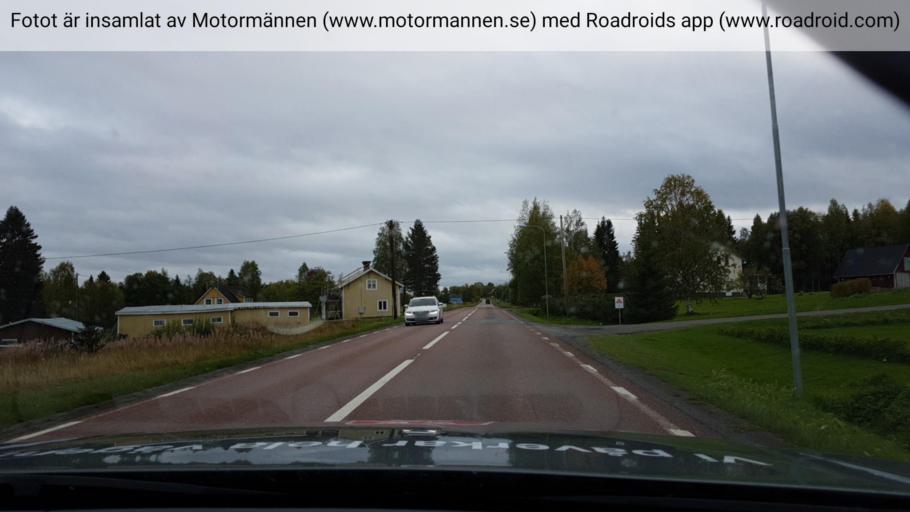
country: SE
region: Jaemtland
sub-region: Stroemsunds Kommun
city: Stroemsund
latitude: 63.8282
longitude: 15.5140
